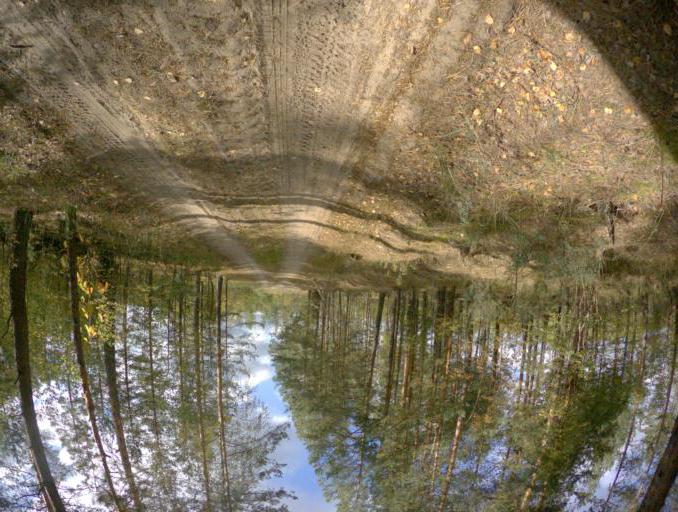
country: RU
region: Moskovskaya
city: Baksheyevo
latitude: 55.7338
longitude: 39.8254
